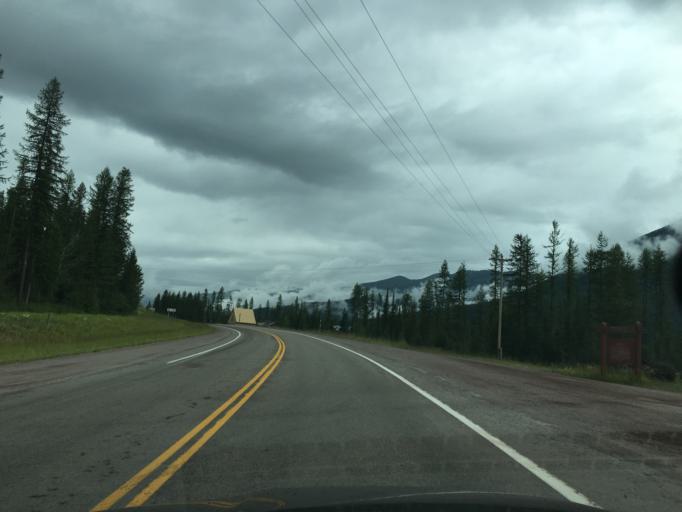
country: US
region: Montana
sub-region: Flathead County
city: Bigfork
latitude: 48.2830
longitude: -113.6064
